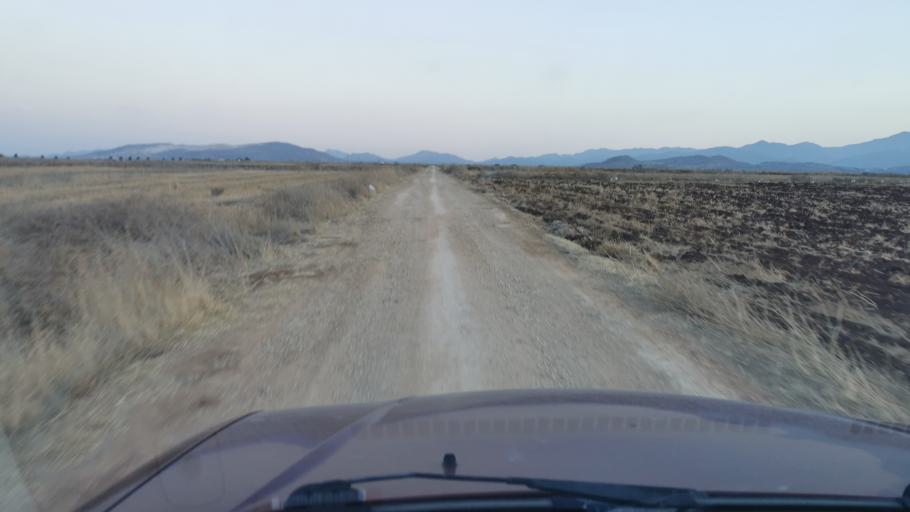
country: CY
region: Lefkosia
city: Peristerona
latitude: 35.0981
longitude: 33.0779
